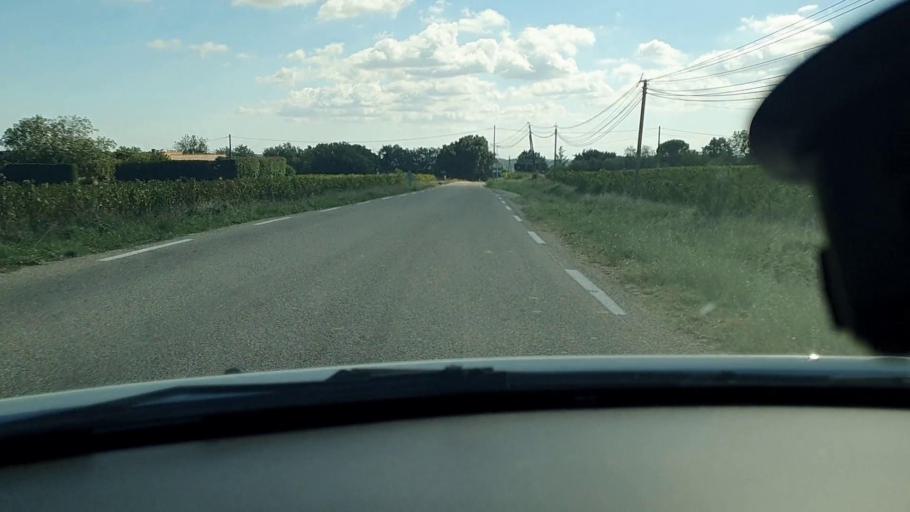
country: FR
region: Languedoc-Roussillon
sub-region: Departement du Gard
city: Sabran
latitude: 44.1508
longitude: 4.4881
